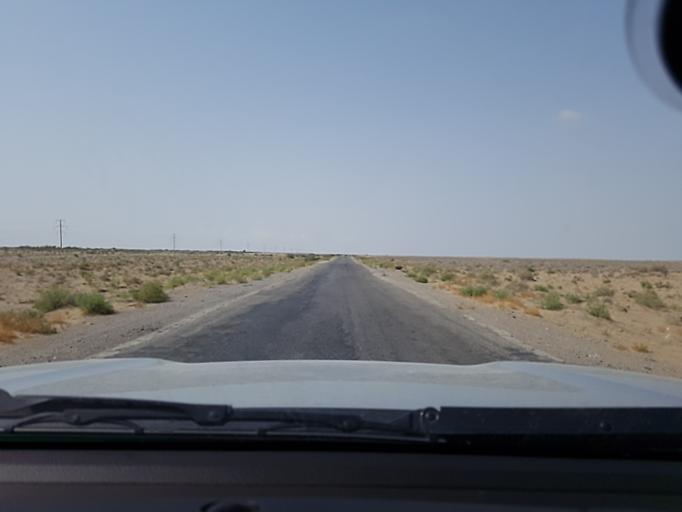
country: TM
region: Balkan
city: Gumdag
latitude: 38.7895
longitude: 54.5974
